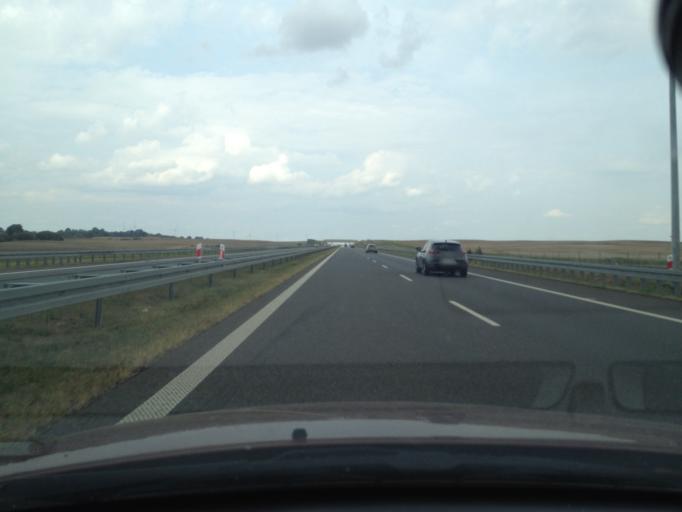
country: PL
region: West Pomeranian Voivodeship
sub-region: Powiat pyrzycki
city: Kozielice
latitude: 53.0582
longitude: 14.8643
